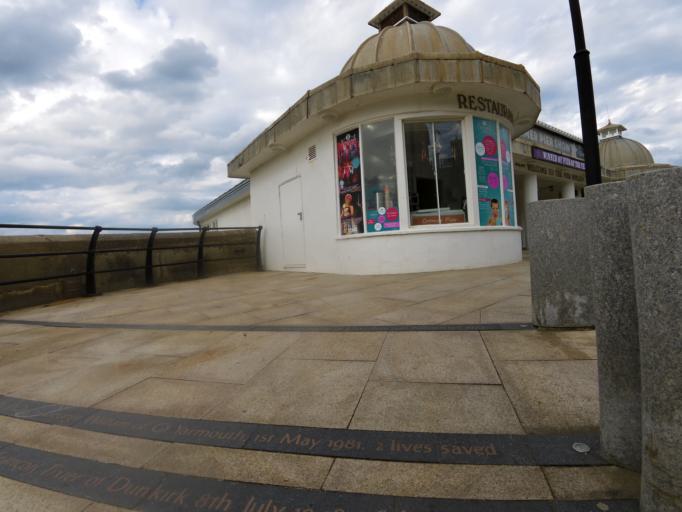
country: GB
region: England
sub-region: Norfolk
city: Cromer
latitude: 52.9328
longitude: 1.3007
